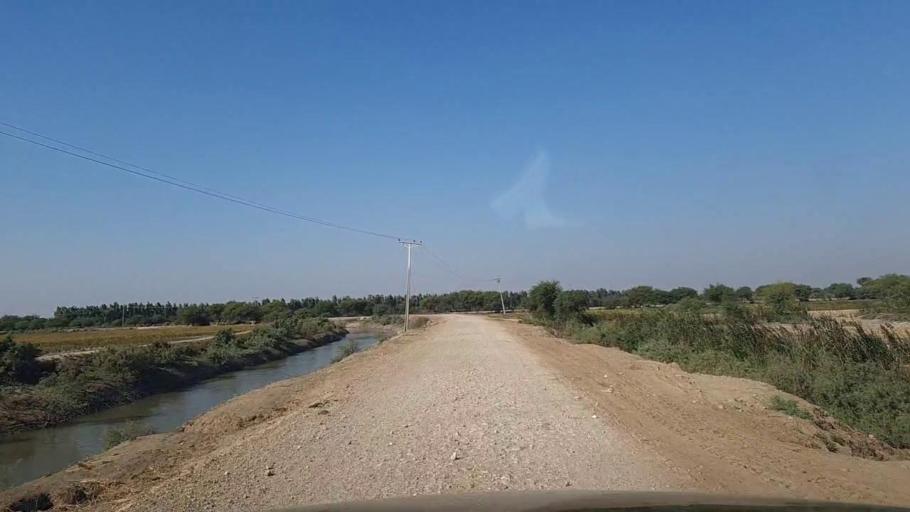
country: PK
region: Sindh
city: Mirpur Batoro
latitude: 24.7336
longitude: 68.3453
